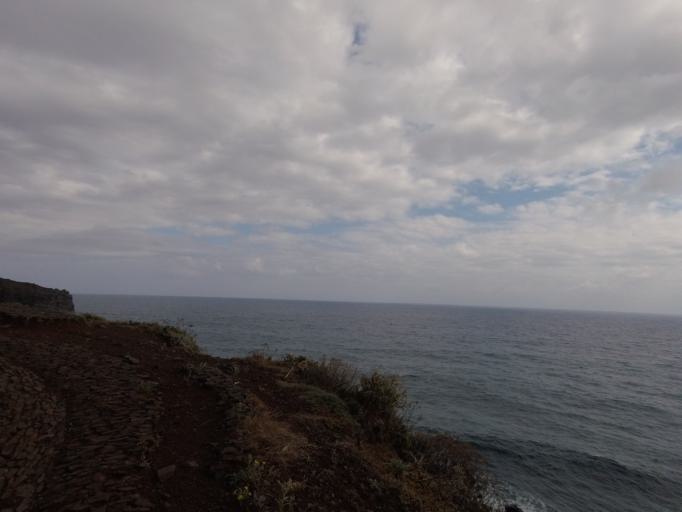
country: PT
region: Madeira
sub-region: Santana
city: Santana
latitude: 32.8341
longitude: -16.9008
